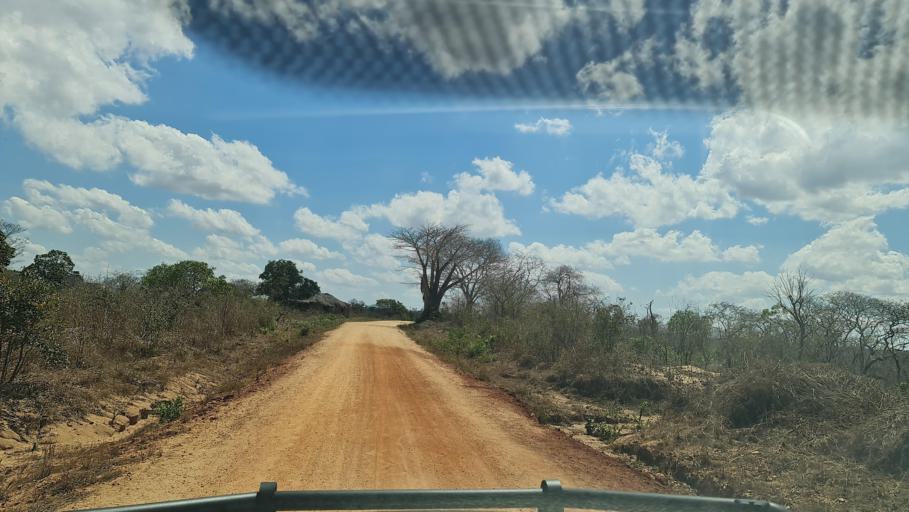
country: MZ
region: Nampula
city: Nacala
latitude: -14.1794
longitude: 40.2235
